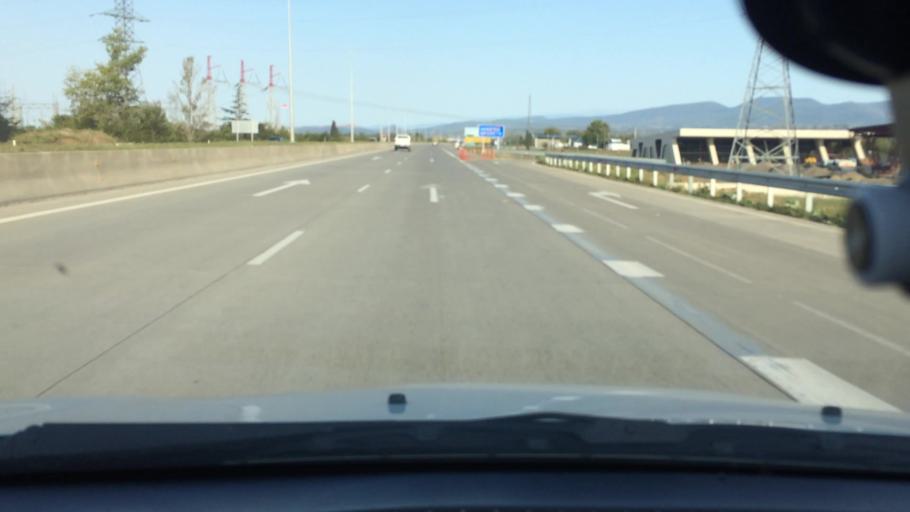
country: GE
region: Imereti
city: Zestap'oni
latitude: 42.1460
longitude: 42.9663
